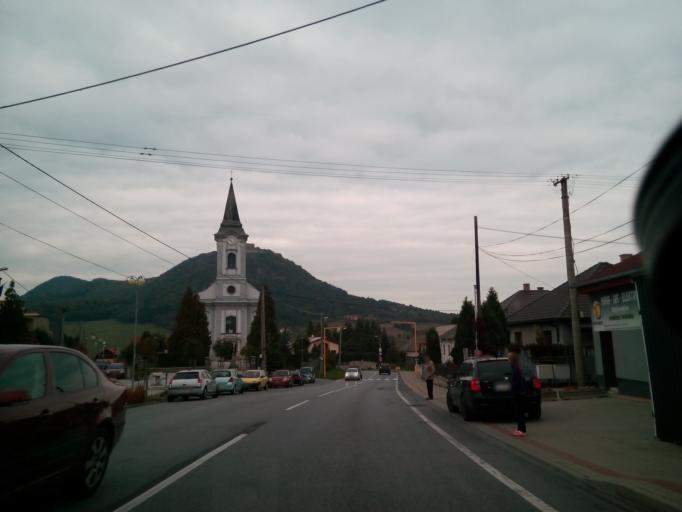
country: SK
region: Presovsky
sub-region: Okres Presov
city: Presov
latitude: 49.0450
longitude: 21.3322
